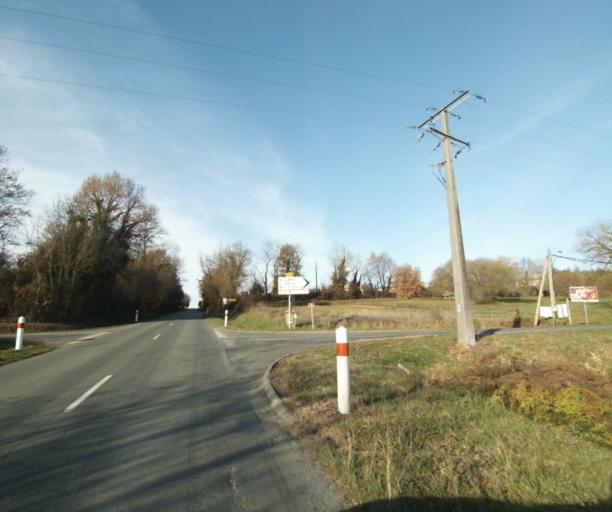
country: FR
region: Poitou-Charentes
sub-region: Departement de la Charente-Maritime
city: Burie
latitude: 45.7976
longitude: -0.4430
